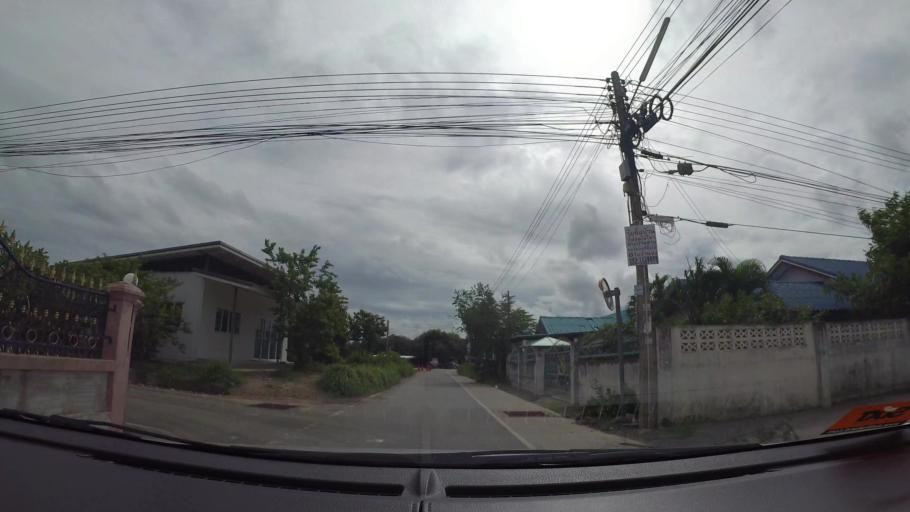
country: TH
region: Chon Buri
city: Sattahip
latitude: 12.7138
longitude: 100.8963
